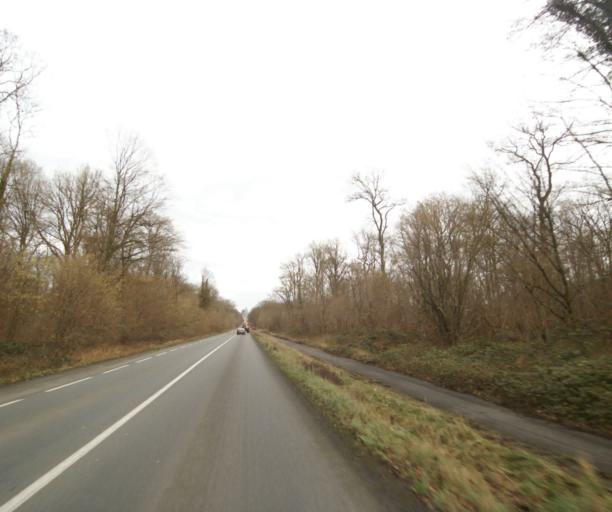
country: BE
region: Wallonia
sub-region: Province du Hainaut
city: Peruwelz
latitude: 50.4831
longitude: 3.6019
